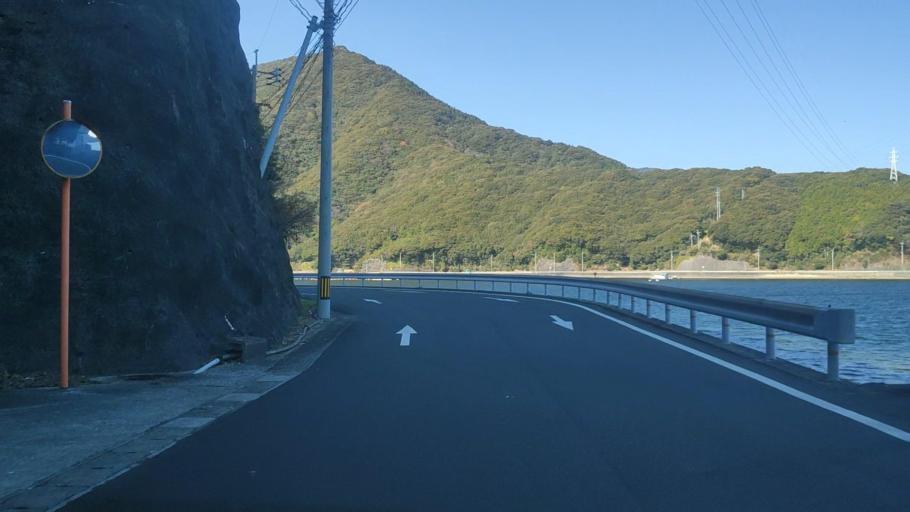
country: JP
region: Oita
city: Saiki
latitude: 32.8365
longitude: 131.9578
